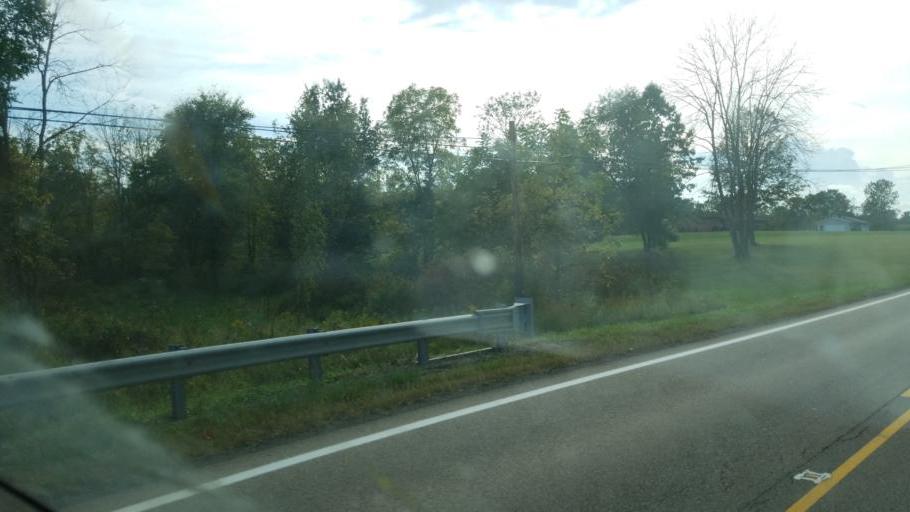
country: US
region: Ohio
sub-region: Knox County
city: Danville
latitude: 40.4511
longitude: -82.2494
